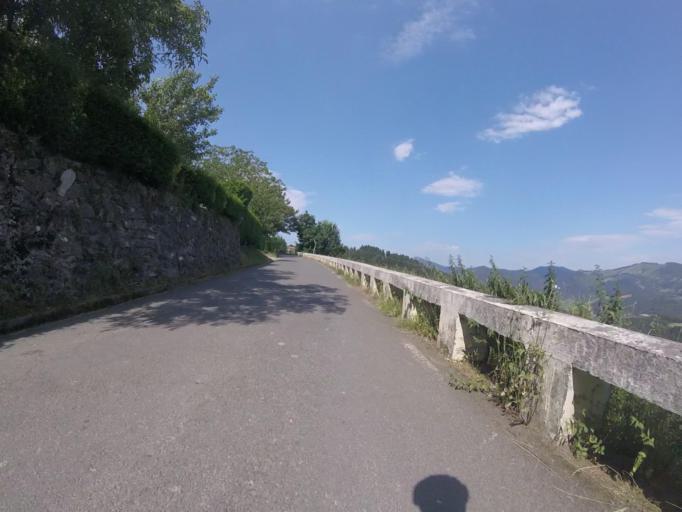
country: ES
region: Basque Country
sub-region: Provincia de Guipuzcoa
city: Orendain
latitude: 43.0816
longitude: -2.1077
